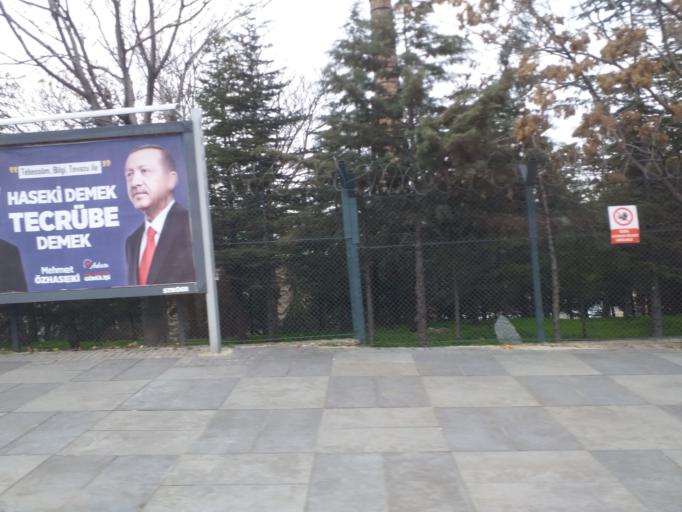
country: TR
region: Ankara
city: Ankara
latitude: 39.9455
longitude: 32.8298
